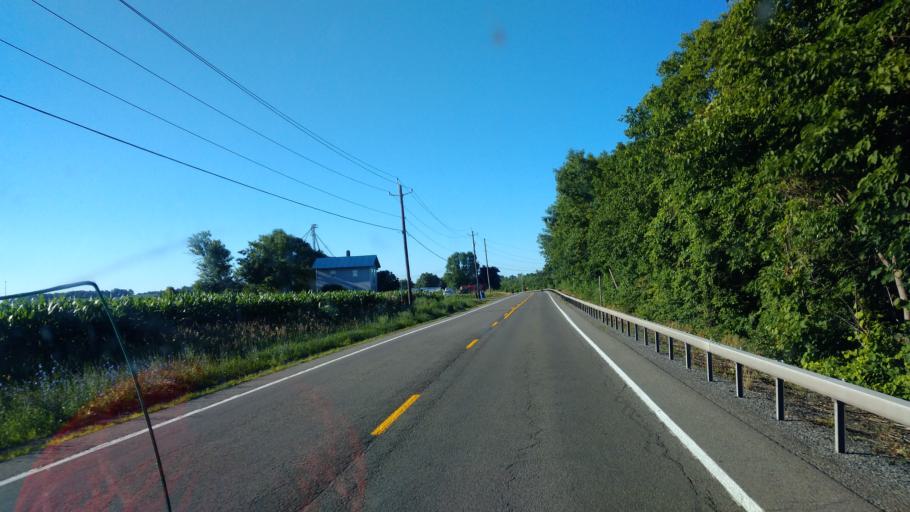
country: US
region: New York
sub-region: Wayne County
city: Lyons
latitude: 43.0419
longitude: -76.9934
